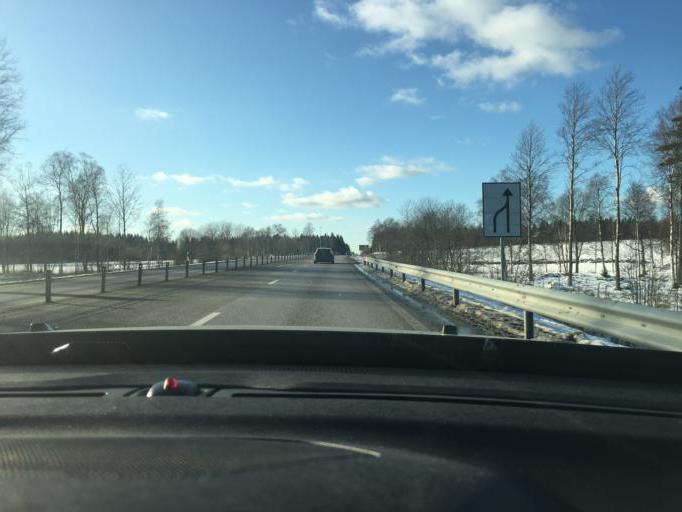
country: SE
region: Vaestra Goetaland
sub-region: Ulricehamns Kommun
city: Ulricehamn
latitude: 57.8007
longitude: 13.5103
